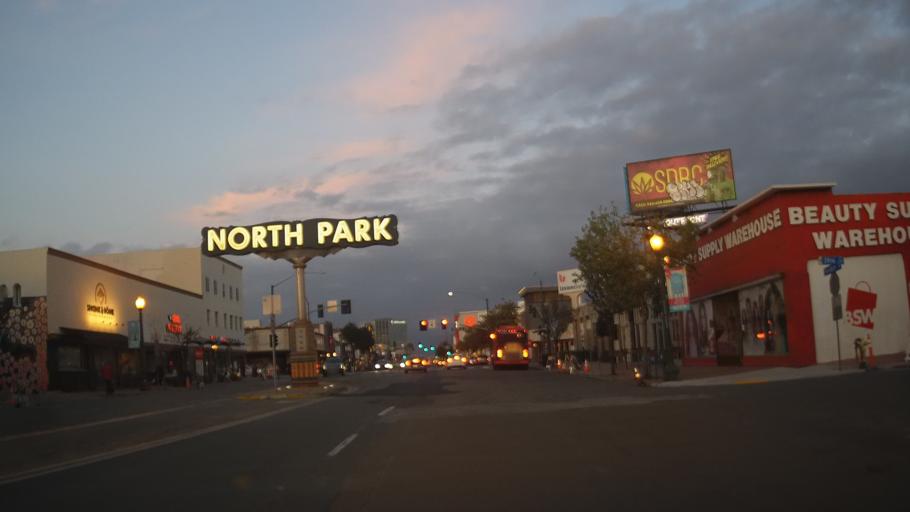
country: US
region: California
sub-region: San Diego County
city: San Diego
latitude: 32.7483
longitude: -117.1312
